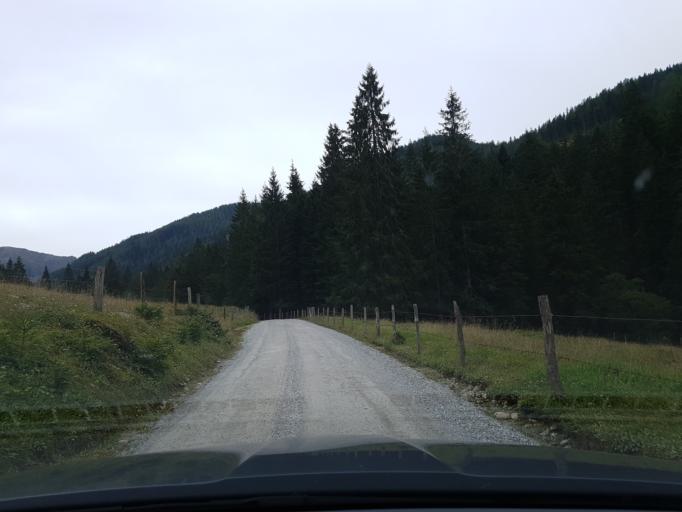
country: AT
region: Salzburg
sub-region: Politischer Bezirk Sankt Johann im Pongau
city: Forstau
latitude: 47.3304
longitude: 13.5772
